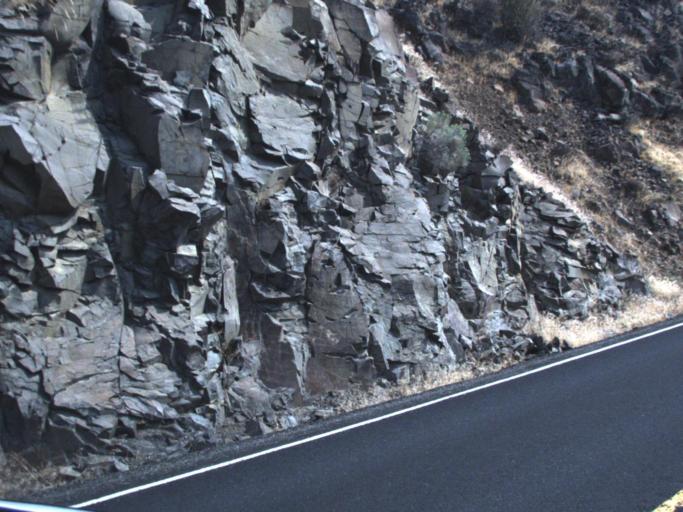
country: US
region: Washington
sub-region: Kittitas County
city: Kittitas
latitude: 46.8404
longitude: -120.4556
